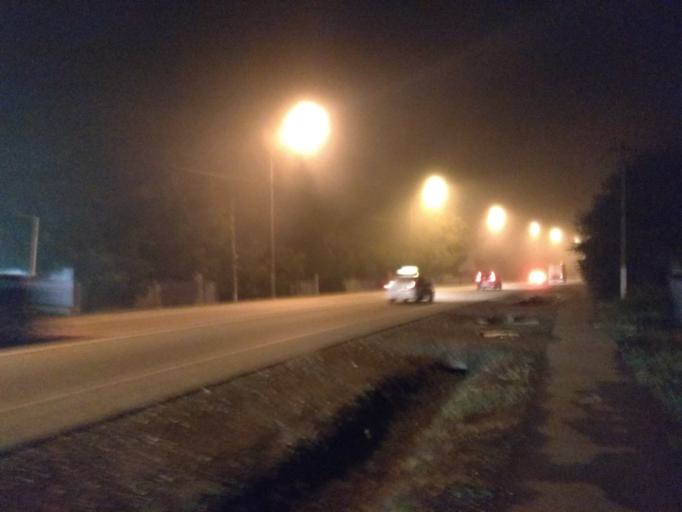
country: RU
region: Krasnodarskiy
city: Kholmskiy
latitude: 44.8466
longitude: 38.3955
